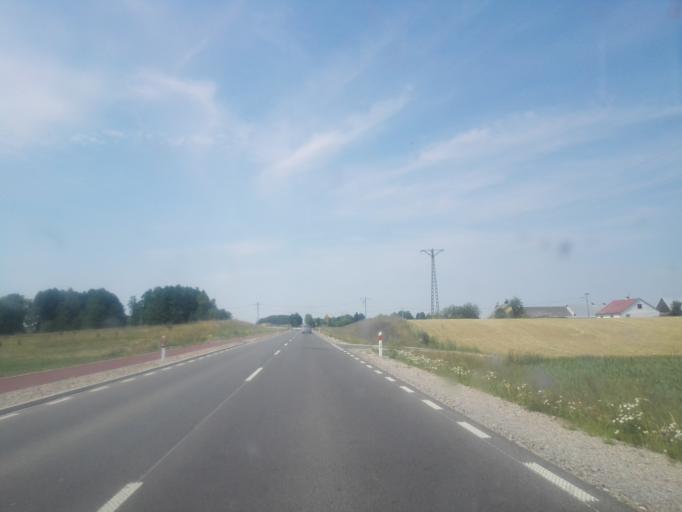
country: PL
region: Podlasie
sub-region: Powiat sejnenski
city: Krasnopol
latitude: 54.1084
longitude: 23.2624
